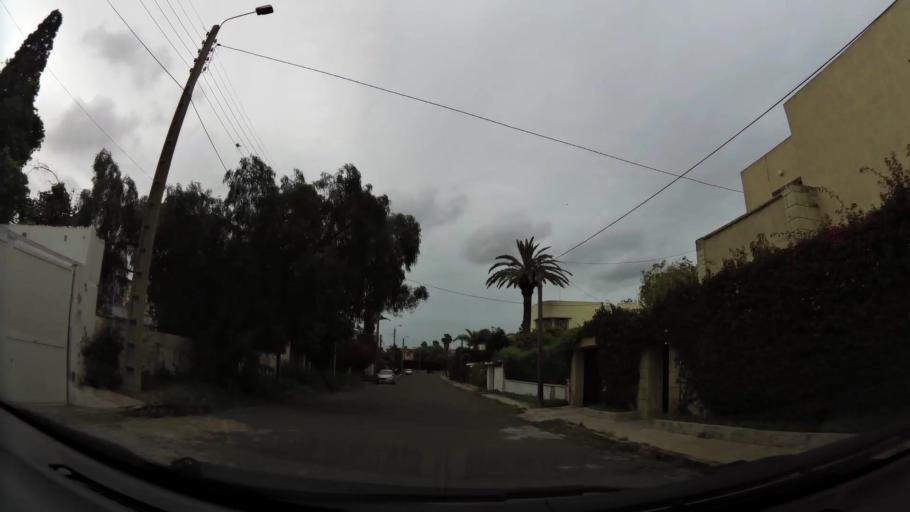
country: MA
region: Grand Casablanca
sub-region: Casablanca
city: Casablanca
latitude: 33.5653
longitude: -7.6228
